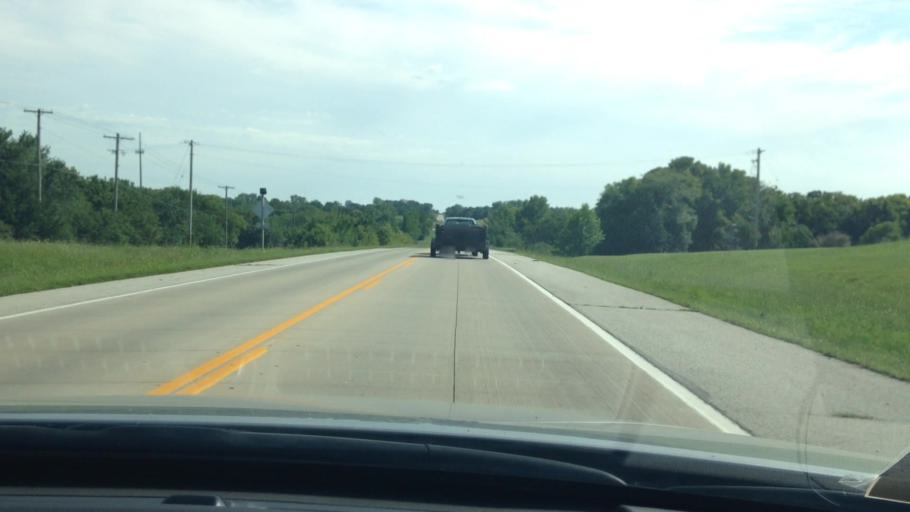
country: US
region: Missouri
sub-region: Cass County
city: Belton
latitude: 38.8246
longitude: -94.5854
